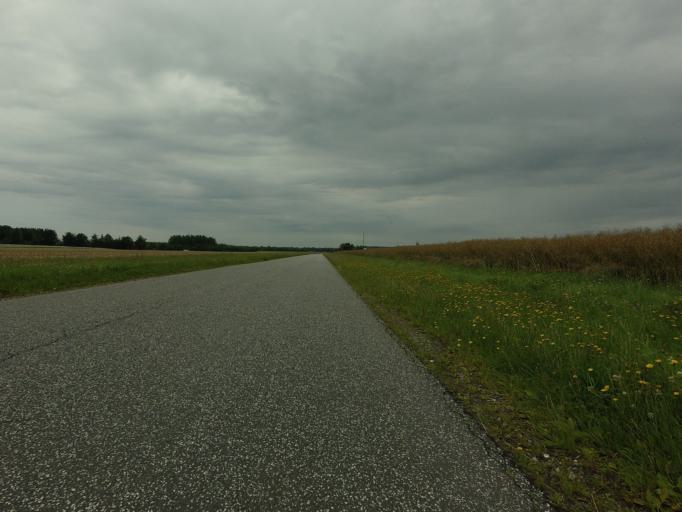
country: DK
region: North Denmark
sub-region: Alborg Kommune
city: Vadum
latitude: 57.1273
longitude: 9.8538
